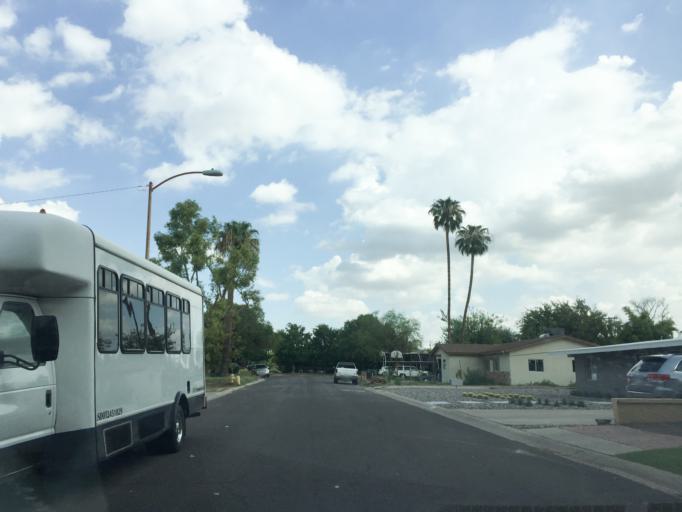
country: US
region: Arizona
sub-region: Maricopa County
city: Phoenix
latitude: 33.5318
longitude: -112.0535
